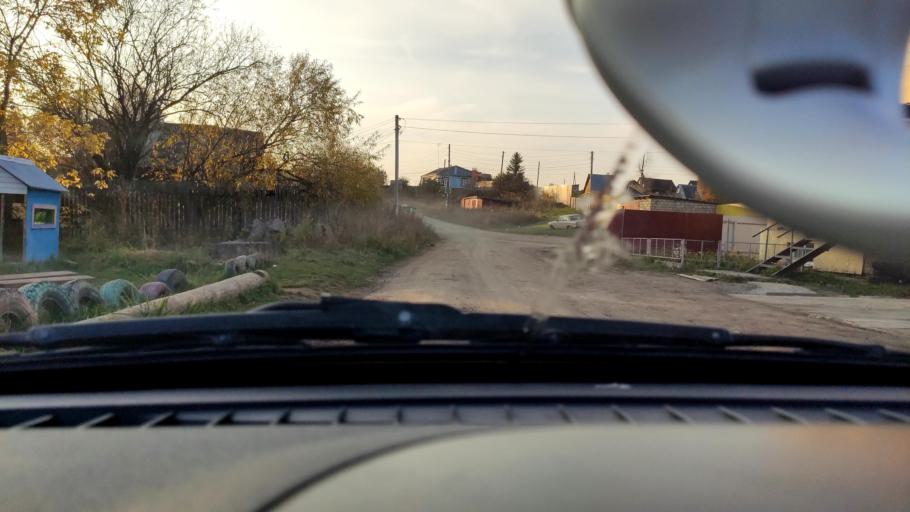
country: RU
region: Perm
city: Lobanovo
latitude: 57.8513
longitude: 56.3413
